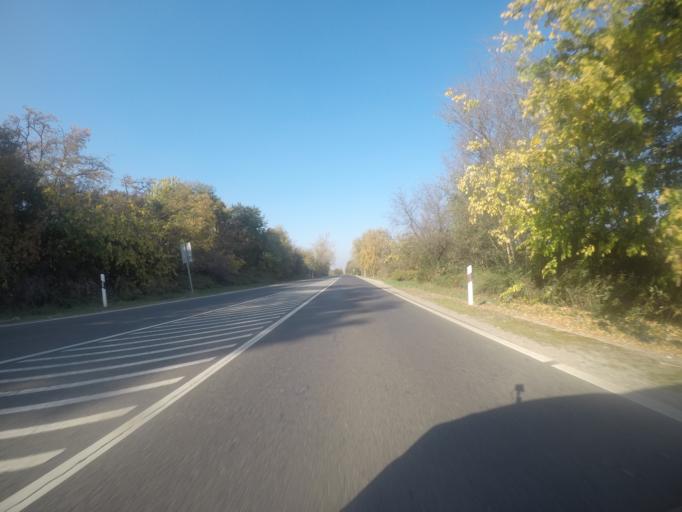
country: HU
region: Pest
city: Szazhalombatta
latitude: 47.3192
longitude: 18.8908
